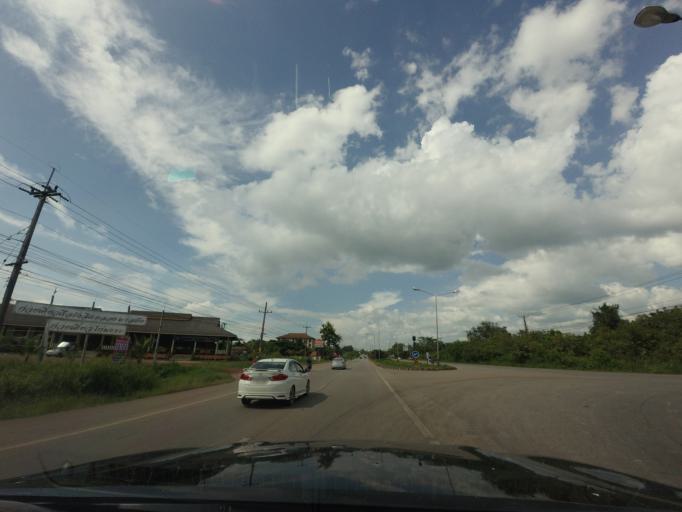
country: TH
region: Nong Khai
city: Sa Khrai
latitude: 17.5609
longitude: 102.8012
